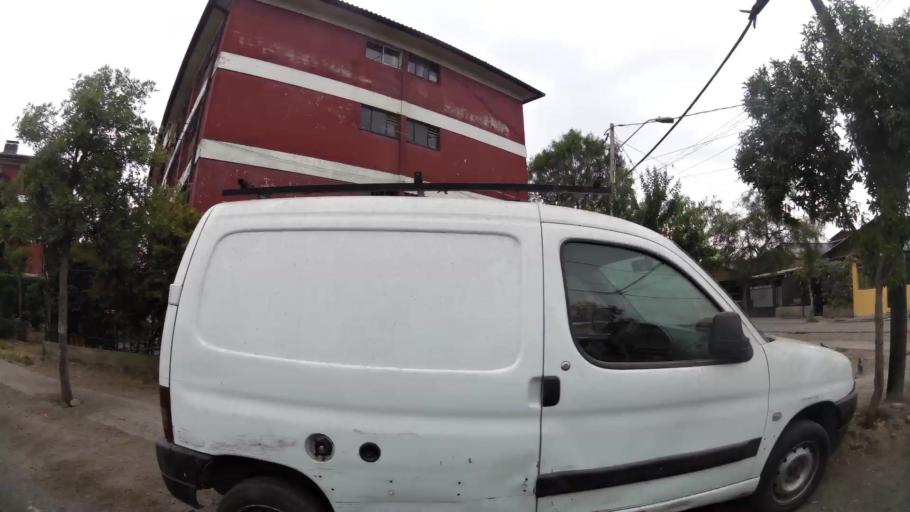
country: CL
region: Santiago Metropolitan
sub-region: Provincia de Maipo
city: San Bernardo
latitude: -33.5241
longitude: -70.6945
